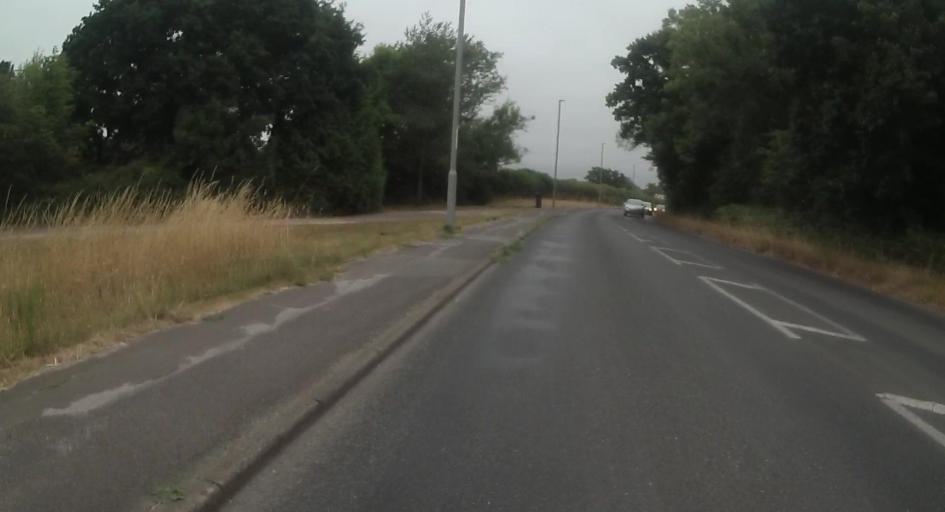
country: GB
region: England
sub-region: Dorset
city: Wareham
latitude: 50.6729
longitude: -2.1075
